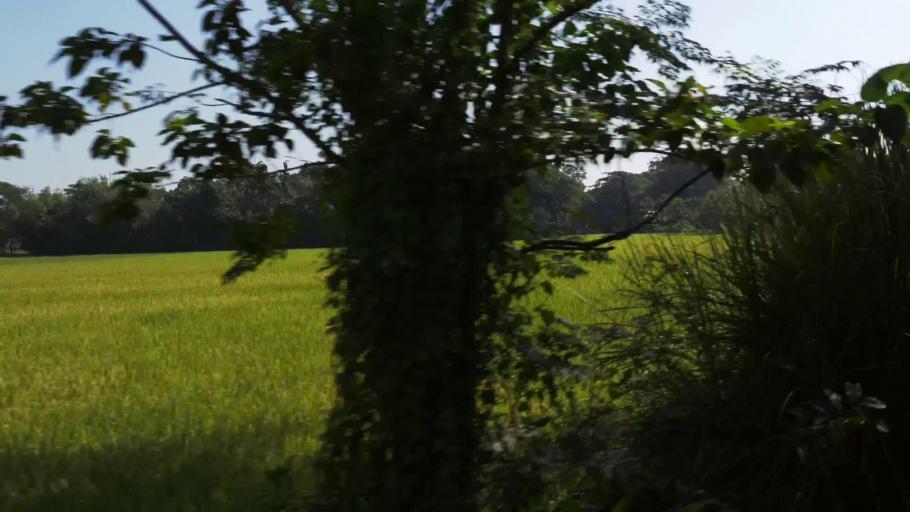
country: BD
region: Dhaka
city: Gafargaon
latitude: 24.5121
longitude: 90.5137
